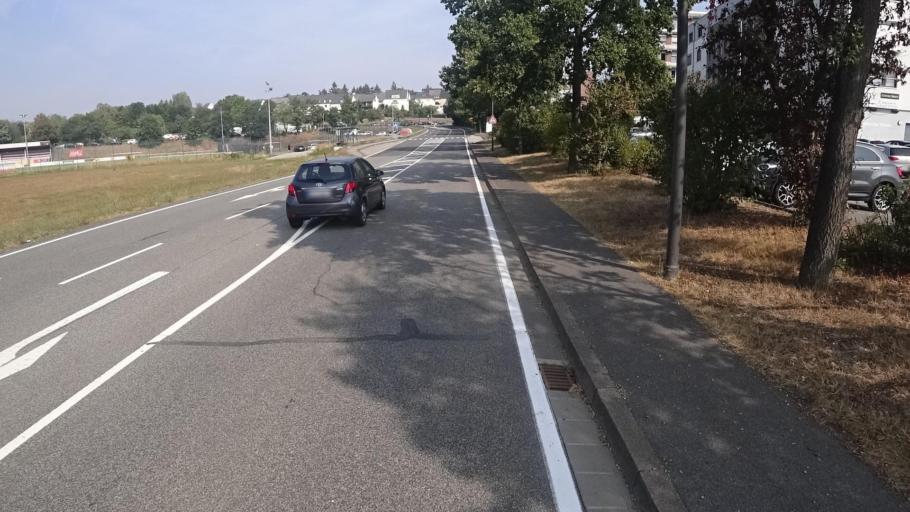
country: DE
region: Rheinland-Pfalz
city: Kumbdchen
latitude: 49.9792
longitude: 7.5168
